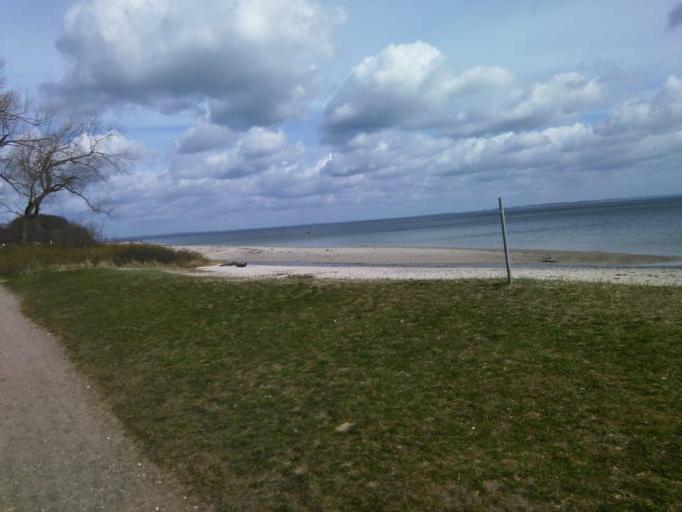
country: DK
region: Central Jutland
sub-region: Arhus Kommune
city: Beder
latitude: 56.0847
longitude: 10.2489
